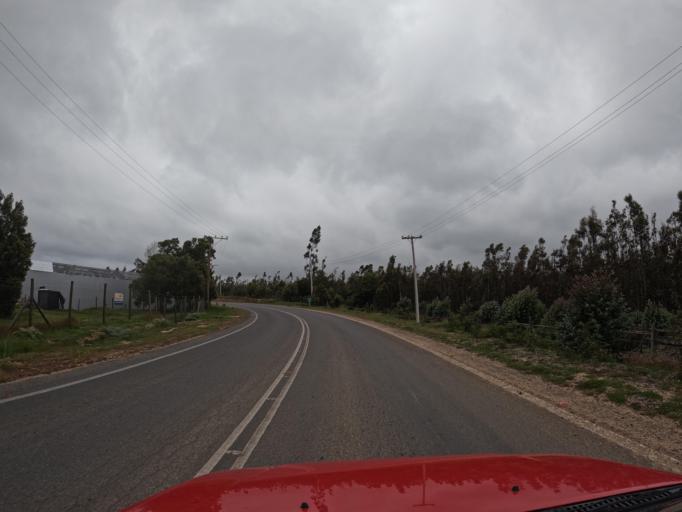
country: CL
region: O'Higgins
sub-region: Provincia de Colchagua
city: Santa Cruz
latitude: -34.5065
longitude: -72.0030
